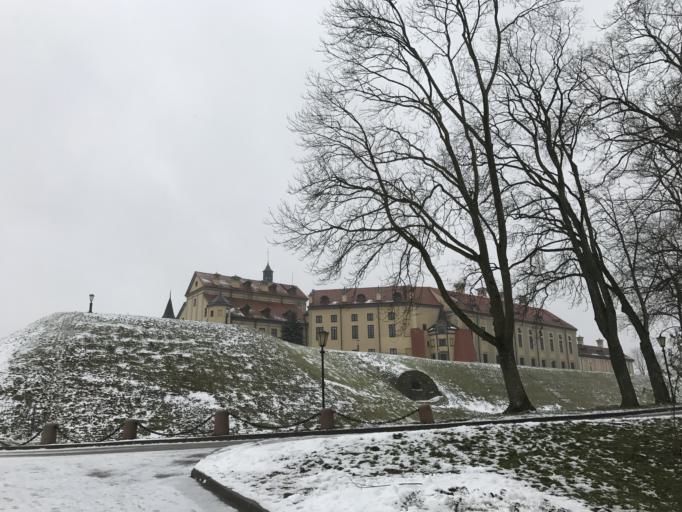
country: BY
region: Minsk
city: Nyasvizh
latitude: 53.2233
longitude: 26.6937
